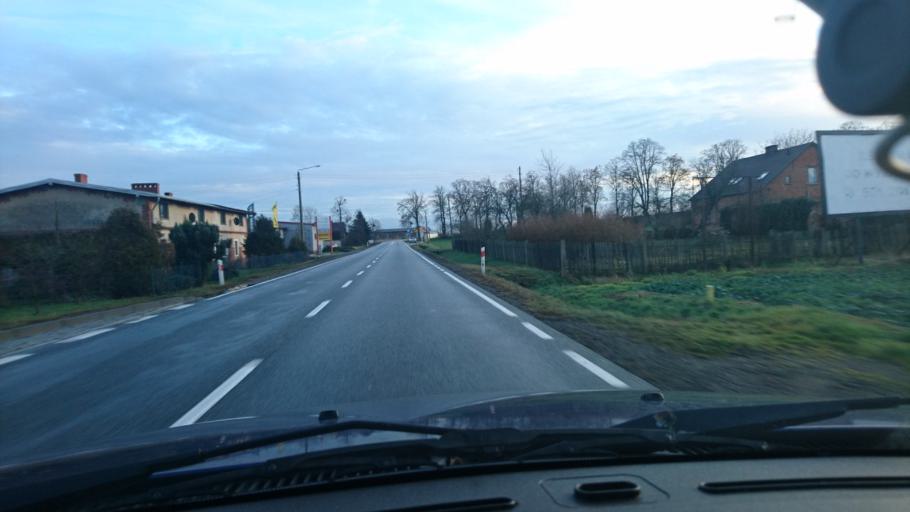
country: PL
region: Opole Voivodeship
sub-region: Powiat kluczborski
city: Byczyna
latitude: 51.1377
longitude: 18.1975
